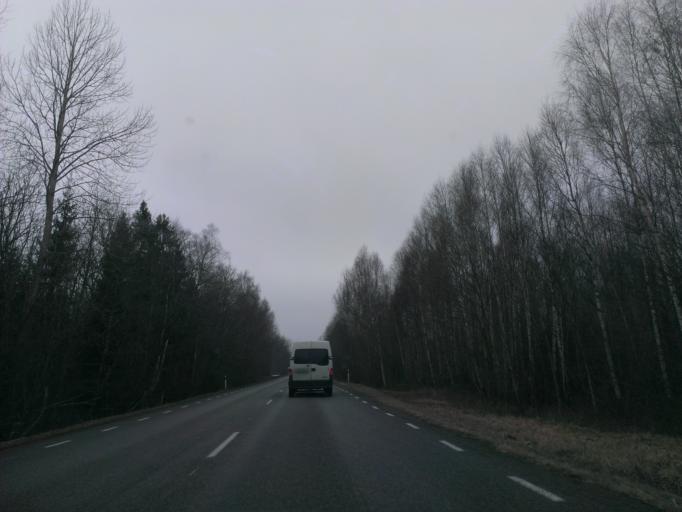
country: EE
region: Paernumaa
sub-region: Audru vald
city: Audru
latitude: 58.4875
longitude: 24.1476
